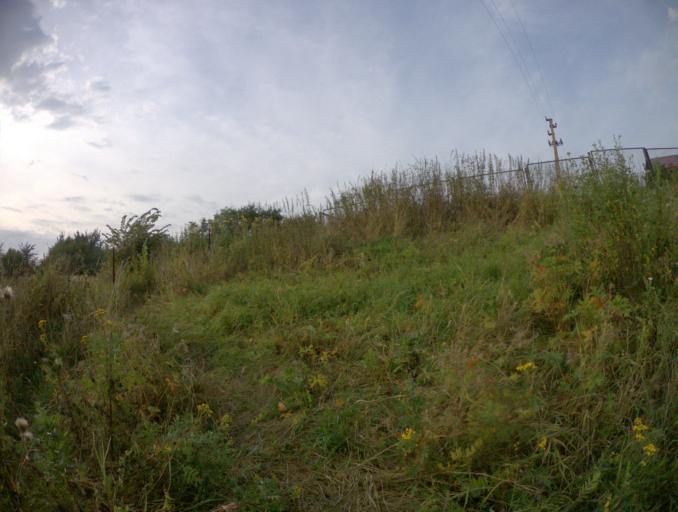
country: RU
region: Vladimir
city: Kideksha
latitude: 56.3494
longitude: 40.5167
